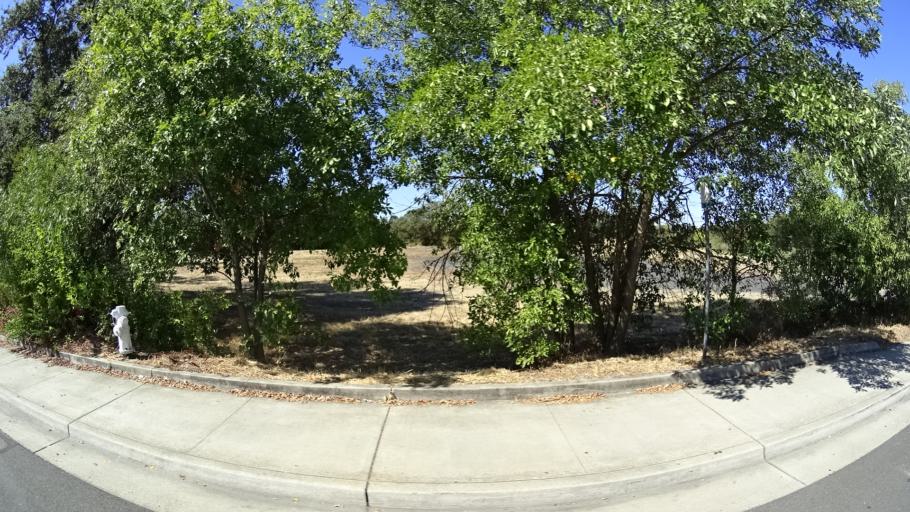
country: US
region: California
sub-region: Sacramento County
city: Elk Grove
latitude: 38.4211
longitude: -121.3717
